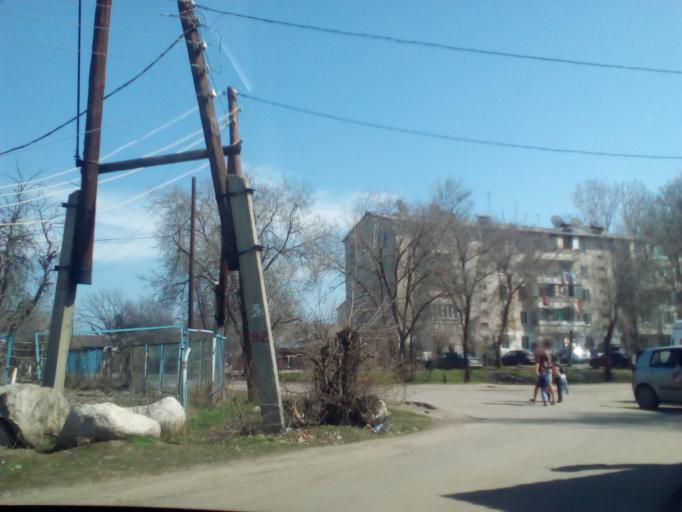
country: KZ
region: Almaty Oblysy
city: Burunday
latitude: 43.1616
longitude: 76.4103
